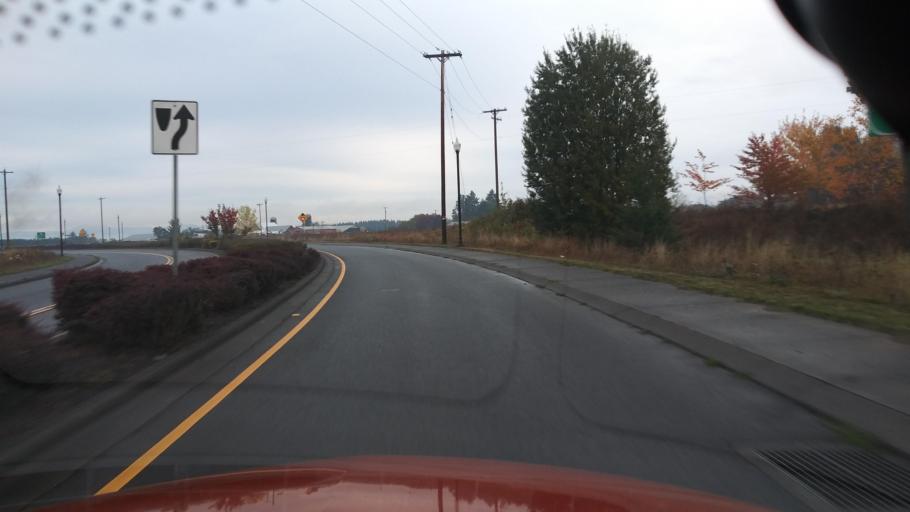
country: US
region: Oregon
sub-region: Washington County
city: Cornelius
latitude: 45.5506
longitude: -123.0620
